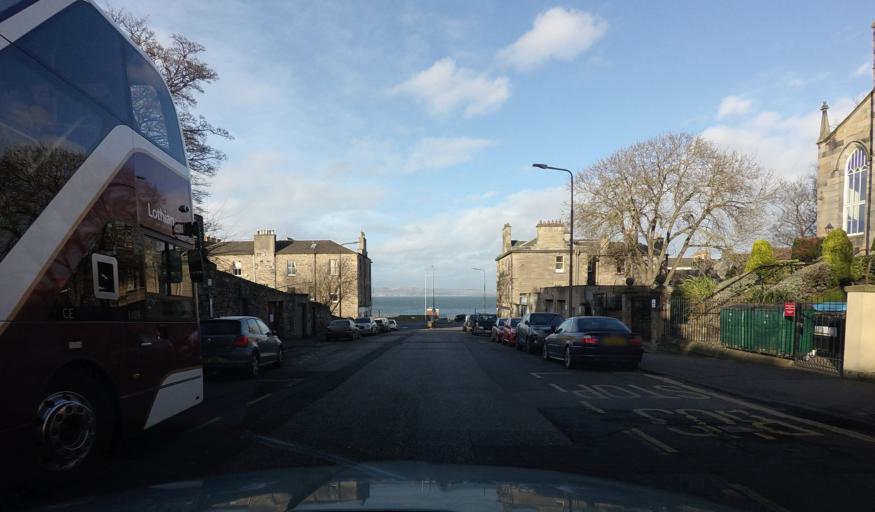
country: GB
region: Scotland
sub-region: Edinburgh
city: Edinburgh
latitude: 55.9796
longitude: -3.1979
